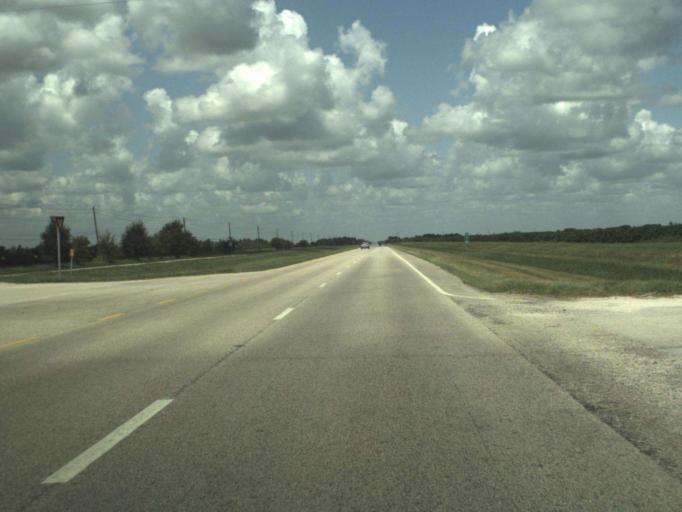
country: US
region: Florida
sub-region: Indian River County
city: Fellsmere
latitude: 27.6404
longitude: -80.6280
